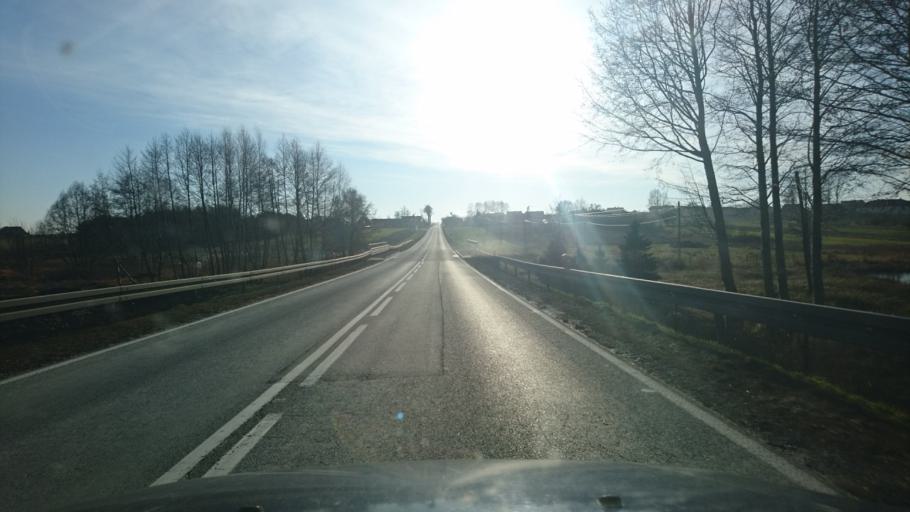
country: PL
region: Opole Voivodeship
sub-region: Powiat oleski
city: Dalachow
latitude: 51.0557
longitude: 18.5989
